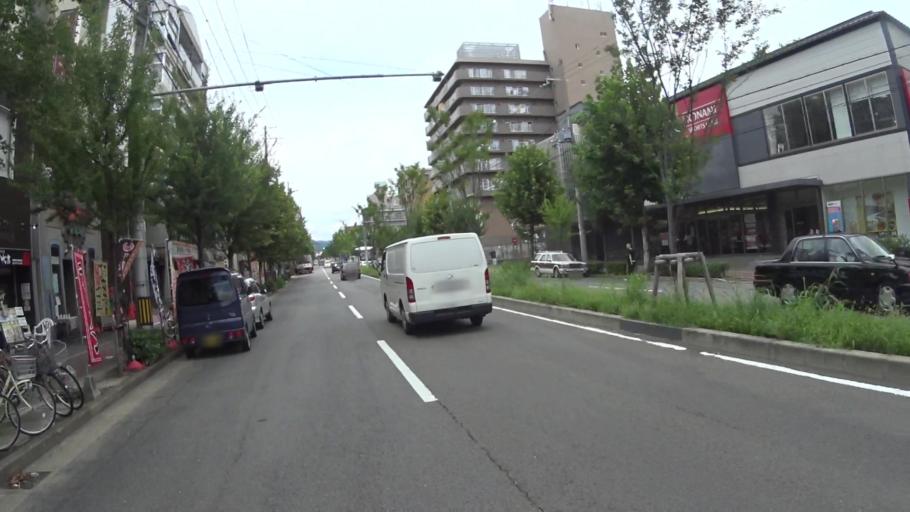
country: JP
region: Kyoto
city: Kyoto
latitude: 35.0117
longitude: 135.7318
